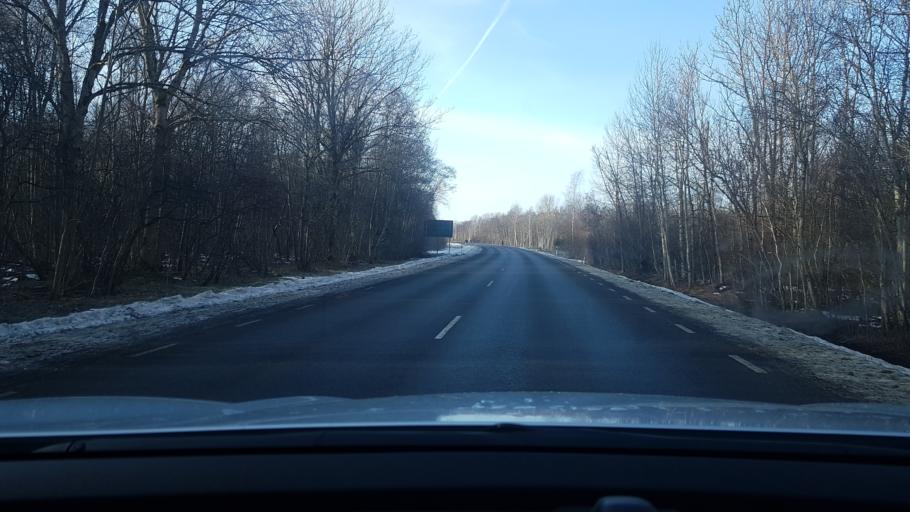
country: EE
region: Saare
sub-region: Kuressaare linn
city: Kuressaare
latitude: 58.2668
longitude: 22.4605
